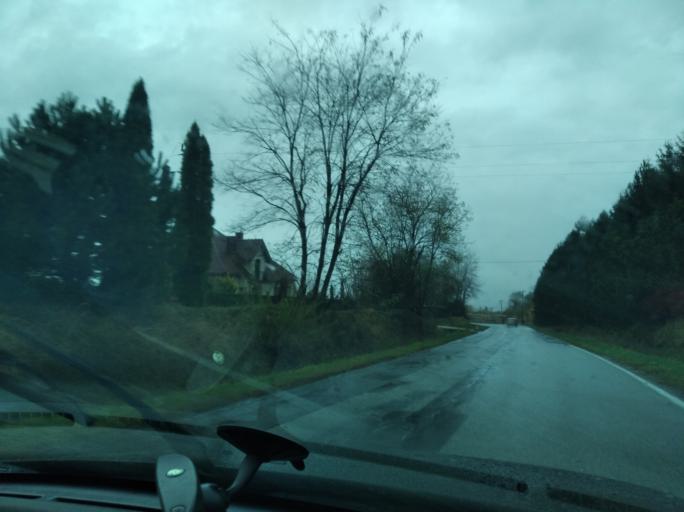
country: PL
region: Subcarpathian Voivodeship
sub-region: Powiat lancucki
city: Handzlowka
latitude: 49.9978
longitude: 22.1977
